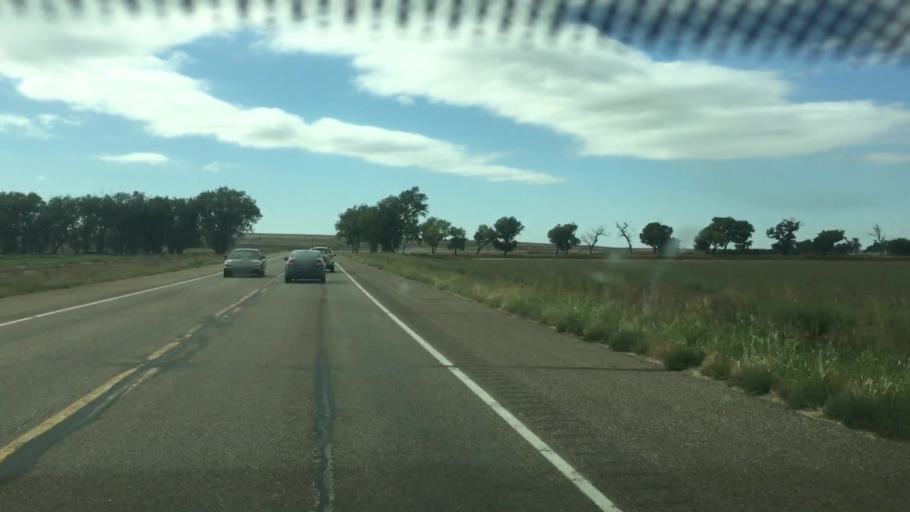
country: US
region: Colorado
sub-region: Prowers County
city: Lamar
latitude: 38.0637
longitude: -102.3529
